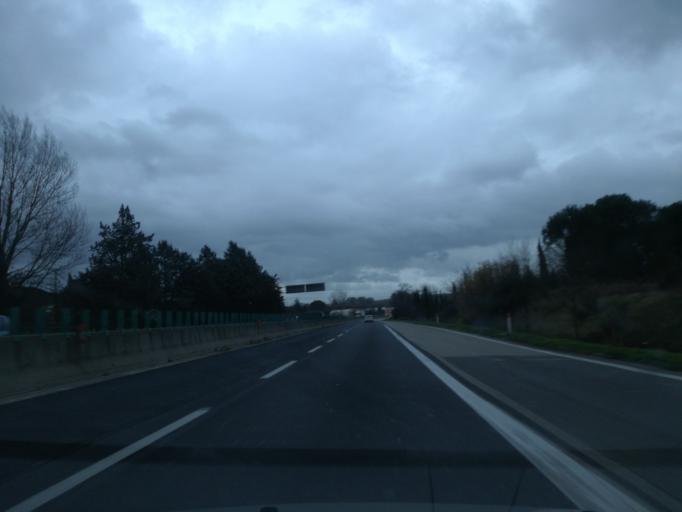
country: IT
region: Umbria
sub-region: Provincia di Perugia
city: Via Lippia
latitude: 43.1073
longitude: 12.4742
